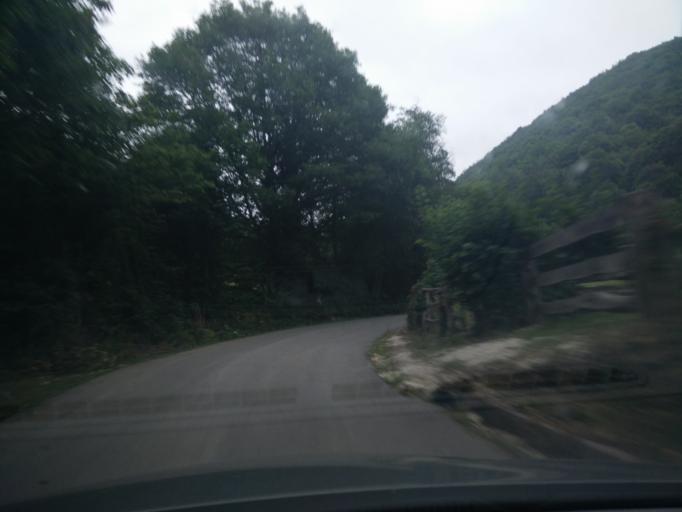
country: ES
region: Asturias
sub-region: Province of Asturias
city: Campo de Caso
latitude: 43.1549
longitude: -5.3926
